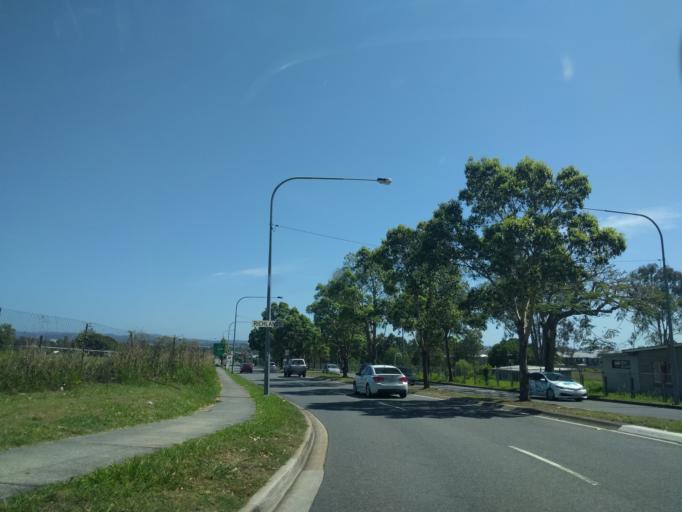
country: AU
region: Queensland
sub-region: Brisbane
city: Richlands
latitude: -27.6009
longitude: 152.9500
